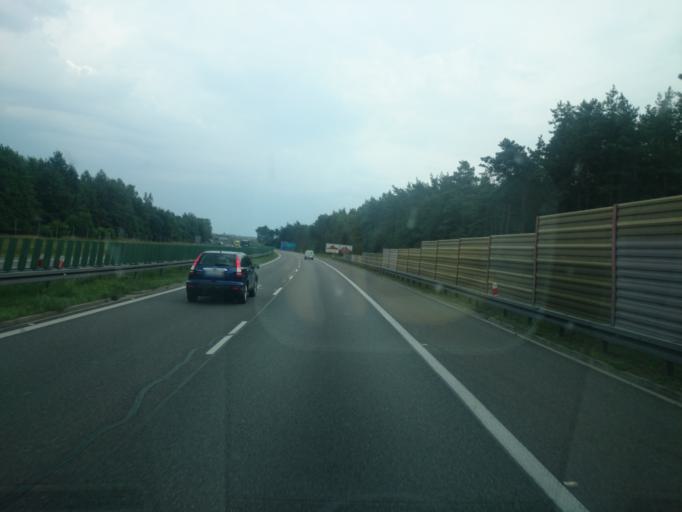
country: PL
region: Opole Voivodeship
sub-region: Powiat krapkowicki
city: Krapkowice
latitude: 50.4943
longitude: 17.9761
